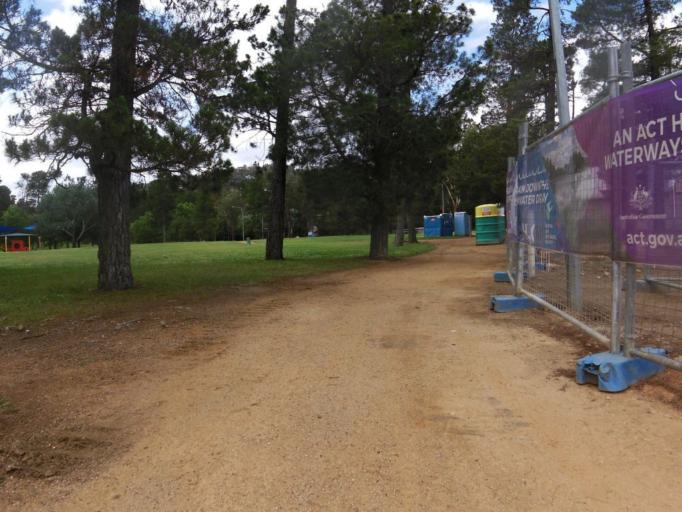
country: AU
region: Australian Capital Territory
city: Macarthur
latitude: -35.4118
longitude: 149.1204
